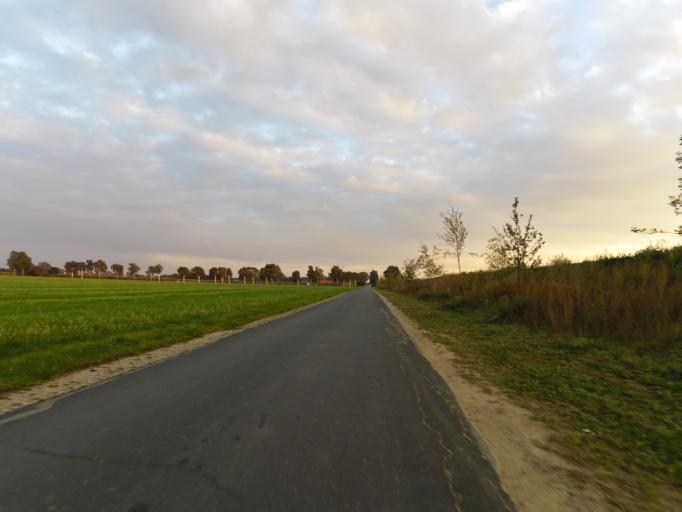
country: NL
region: Gelderland
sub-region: Gemeente Doetinchem
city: Doetinchem
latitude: 51.9521
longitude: 6.2297
